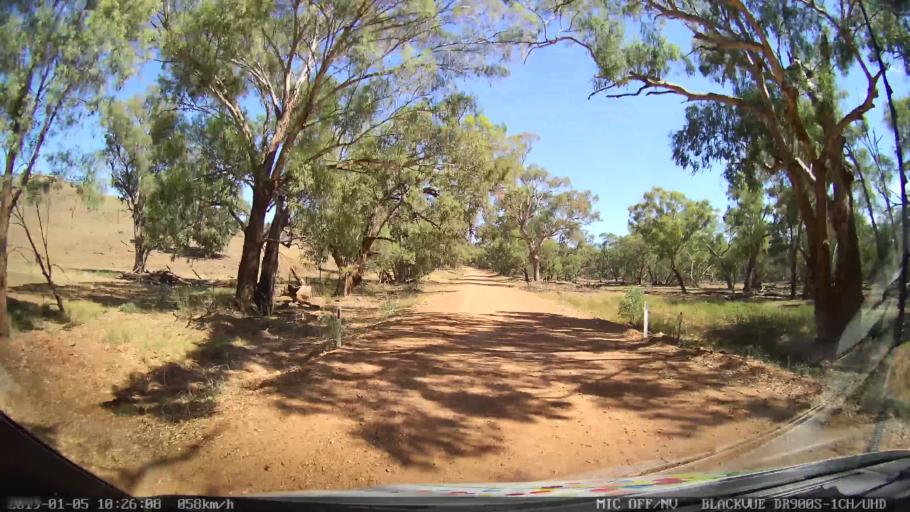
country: AU
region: New South Wales
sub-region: Gilgandra
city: Gilgandra
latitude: -31.5559
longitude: 148.9563
